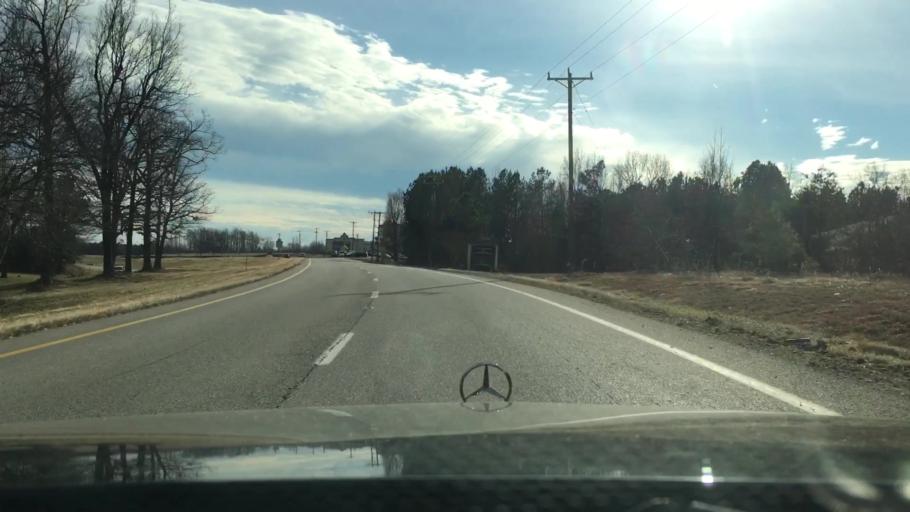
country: US
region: Virginia
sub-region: Pittsylvania County
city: Mount Hermon
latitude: 36.7259
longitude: -79.3849
